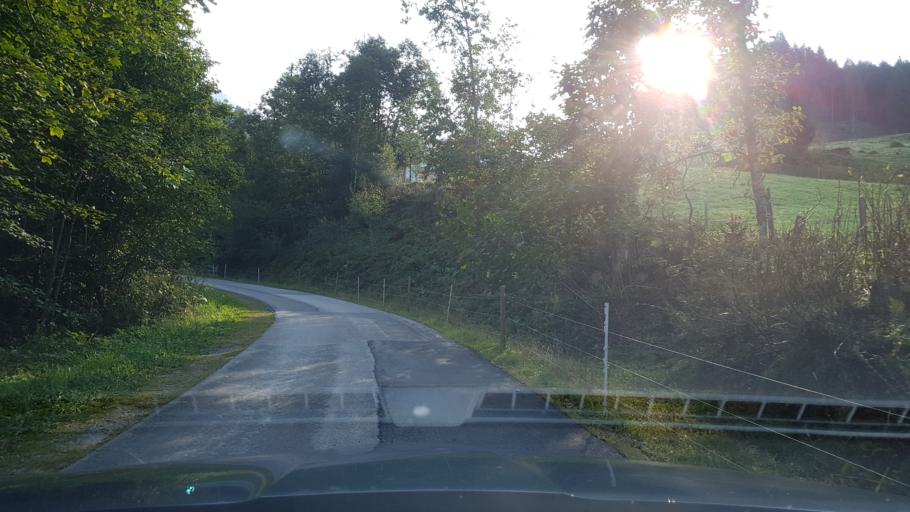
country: AT
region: Salzburg
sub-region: Politischer Bezirk Sankt Johann im Pongau
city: Sankt Johann im Pongau
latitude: 47.2762
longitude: 13.2327
